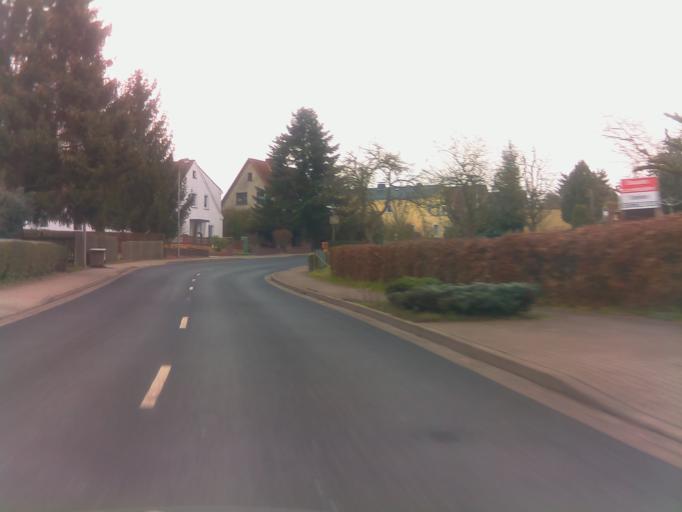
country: DE
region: Thuringia
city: Unterbreizbach
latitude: 50.7929
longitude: 9.9983
